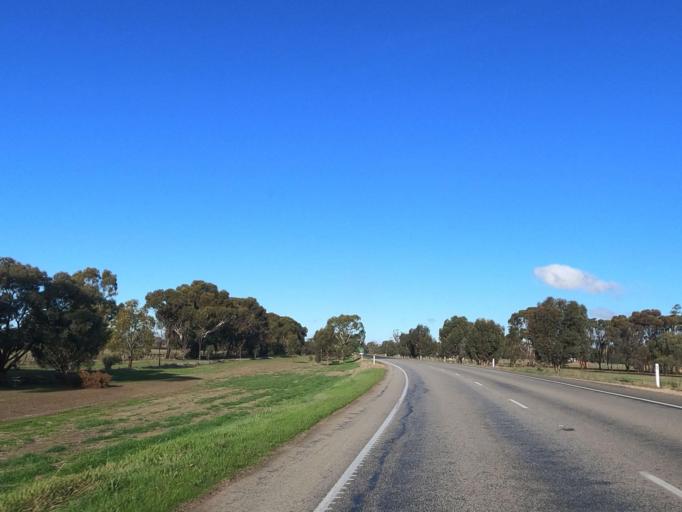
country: AU
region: Victoria
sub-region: Swan Hill
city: Swan Hill
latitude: -35.7289
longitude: 143.8925
